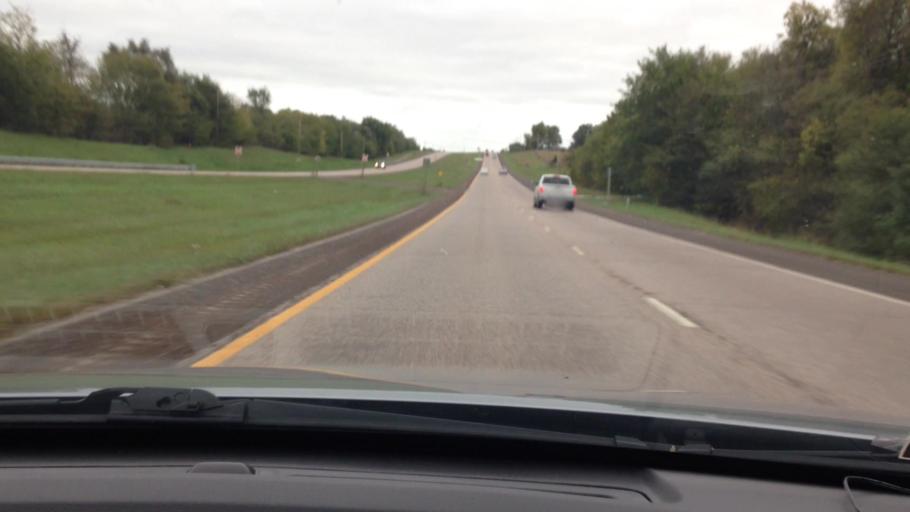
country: US
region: Kansas
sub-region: Leavenworth County
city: Lansing
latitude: 39.2002
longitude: -94.9004
